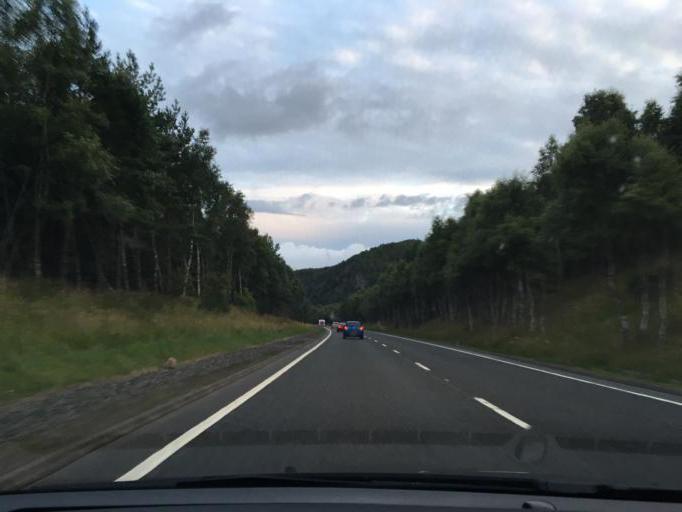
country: GB
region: Scotland
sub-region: Highland
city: Aviemore
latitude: 57.1947
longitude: -3.8364
